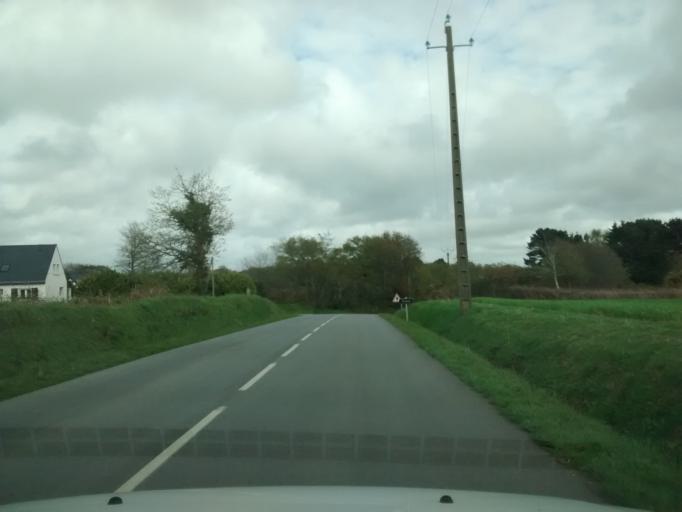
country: FR
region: Brittany
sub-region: Departement du Morbihan
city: Guidel-Plage
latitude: 47.7949
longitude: -3.5073
